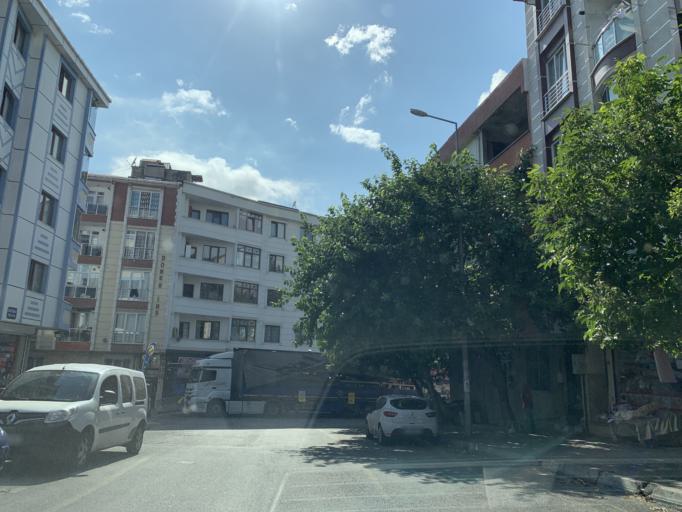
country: TR
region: Istanbul
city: Esenyurt
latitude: 41.0334
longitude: 28.6700
